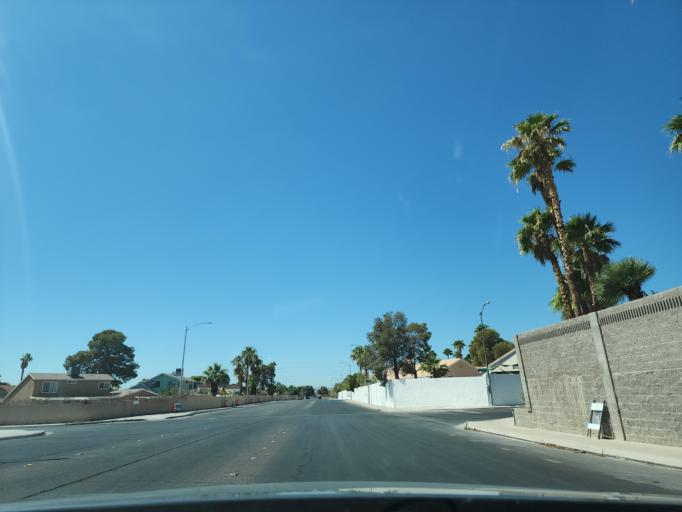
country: US
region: Nevada
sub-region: Clark County
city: Spring Valley
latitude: 36.1187
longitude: -115.2521
